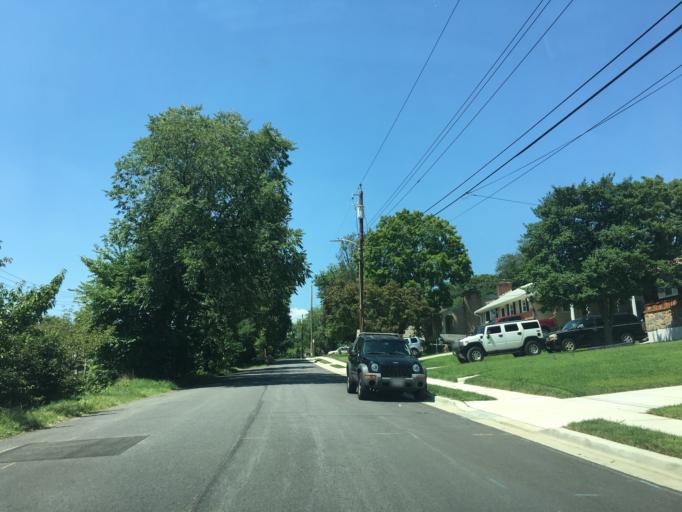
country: US
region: Maryland
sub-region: Anne Arundel County
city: Ferndale
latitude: 39.1891
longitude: -76.6448
